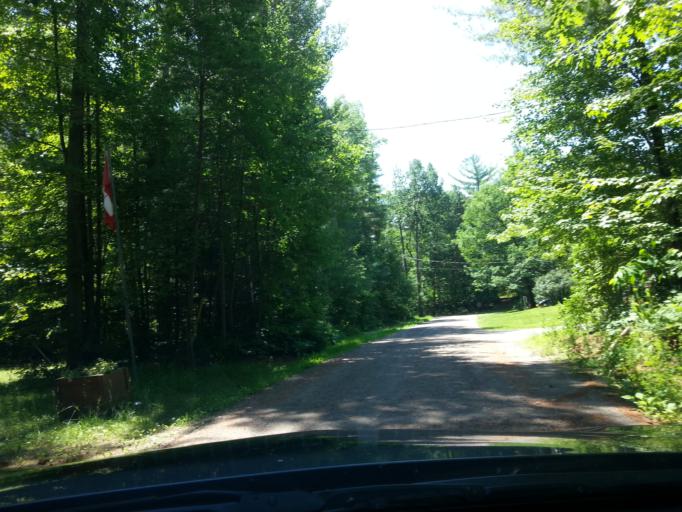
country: CA
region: Ontario
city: Arnprior
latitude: 45.5182
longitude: -76.4126
